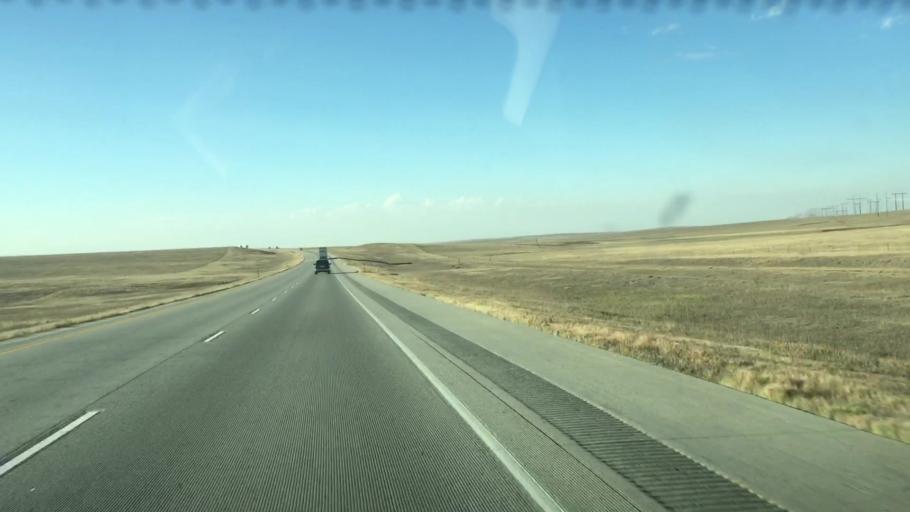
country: US
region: Colorado
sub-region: Lincoln County
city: Limon
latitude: 39.4093
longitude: -103.8991
